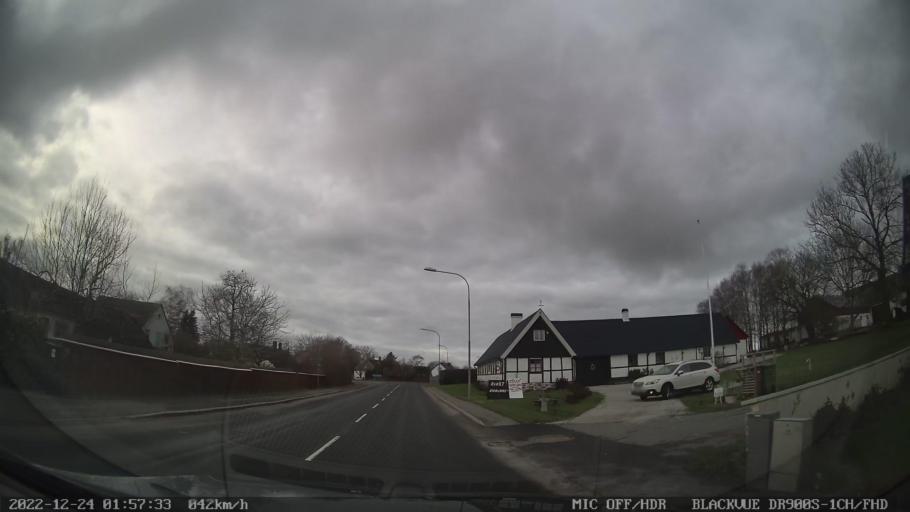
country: SE
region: Skane
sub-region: Tomelilla Kommun
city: Tomelilla
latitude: 55.5999
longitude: 14.0450
